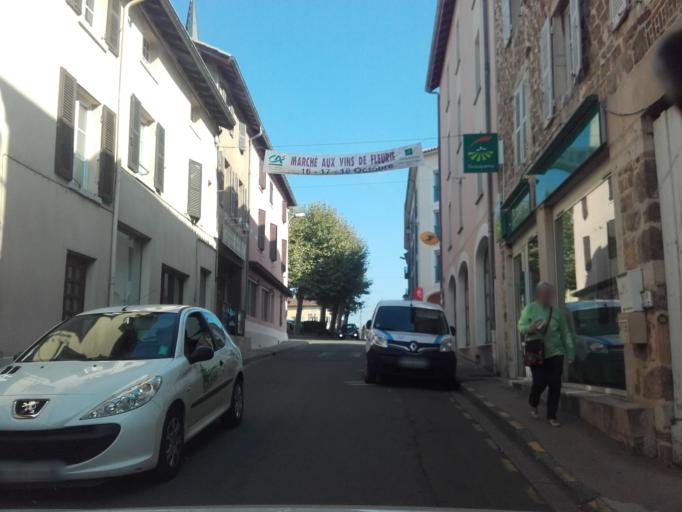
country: FR
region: Rhone-Alpes
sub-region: Departement du Rhone
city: Fleurie
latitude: 46.1918
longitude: 4.6969
